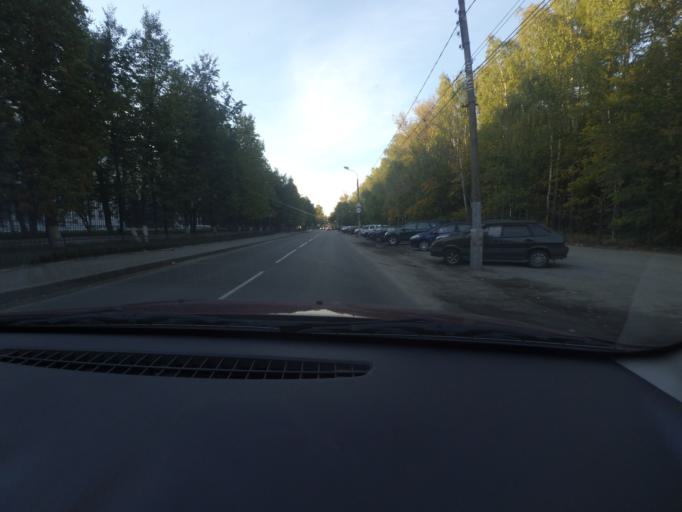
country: RU
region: Nizjnij Novgorod
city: Nizhniy Novgorod
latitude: 56.2701
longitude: 43.9941
